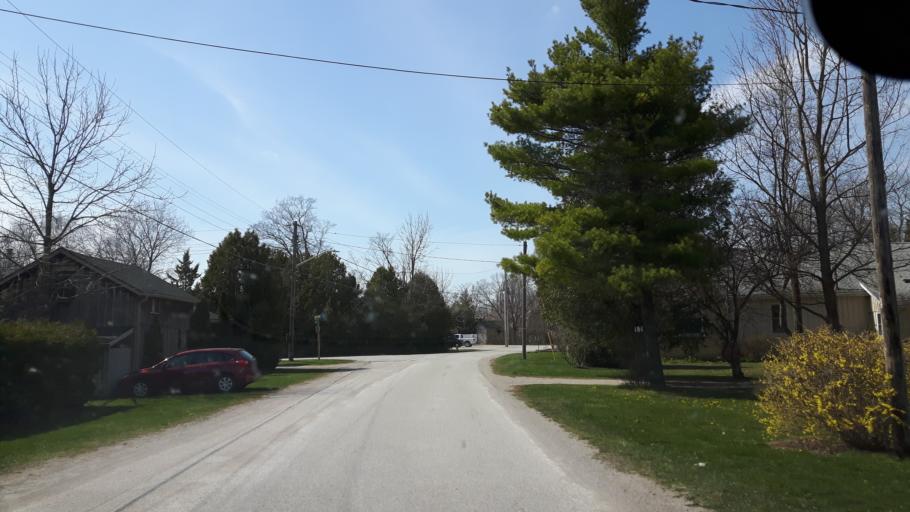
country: CA
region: Ontario
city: Bluewater
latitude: 43.5610
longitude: -81.6947
